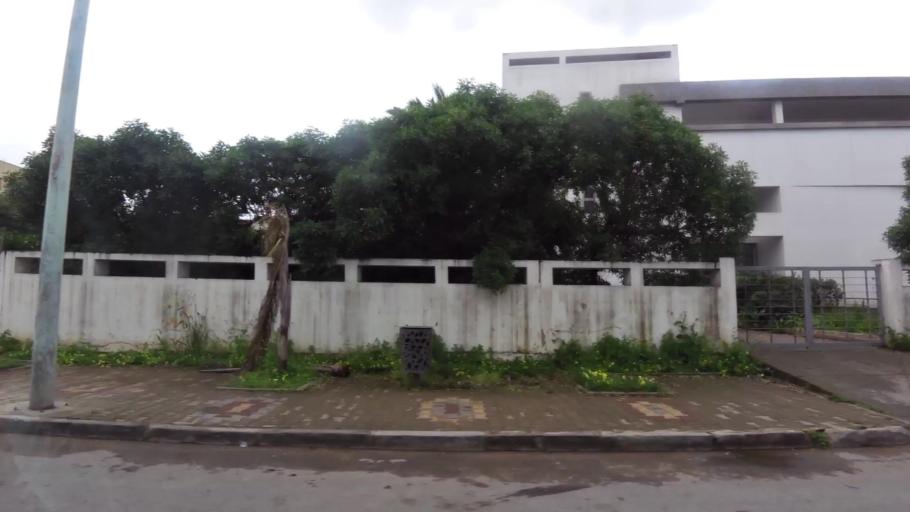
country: MA
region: Grand Casablanca
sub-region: Nouaceur
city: Bouskoura
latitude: 33.5220
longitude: -7.6514
